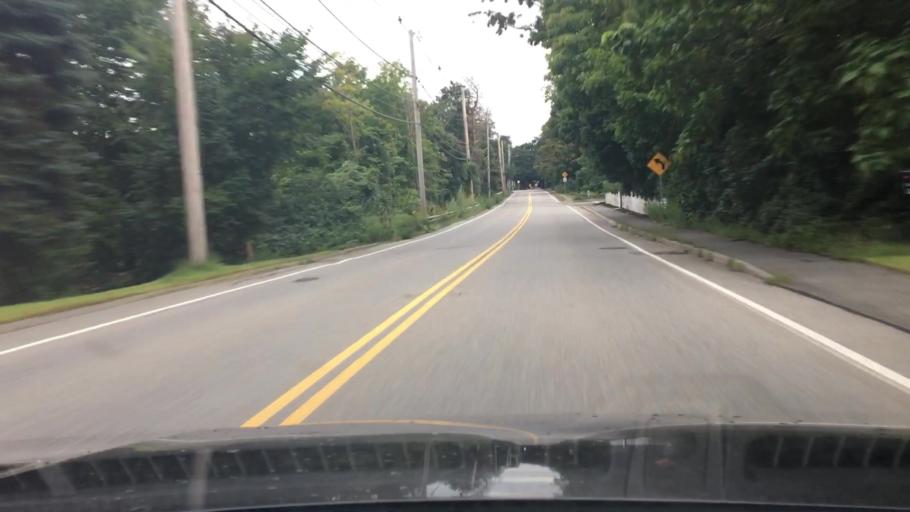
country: US
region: Massachusetts
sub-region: Middlesex County
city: North Reading
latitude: 42.5772
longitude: -71.0658
